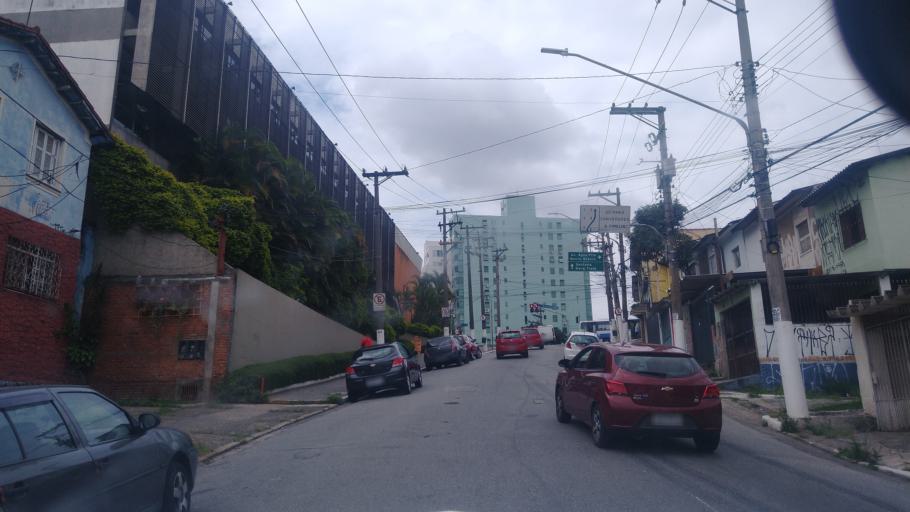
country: BR
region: Sao Paulo
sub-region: Sao Paulo
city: Sao Paulo
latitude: -23.4767
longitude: -46.6098
